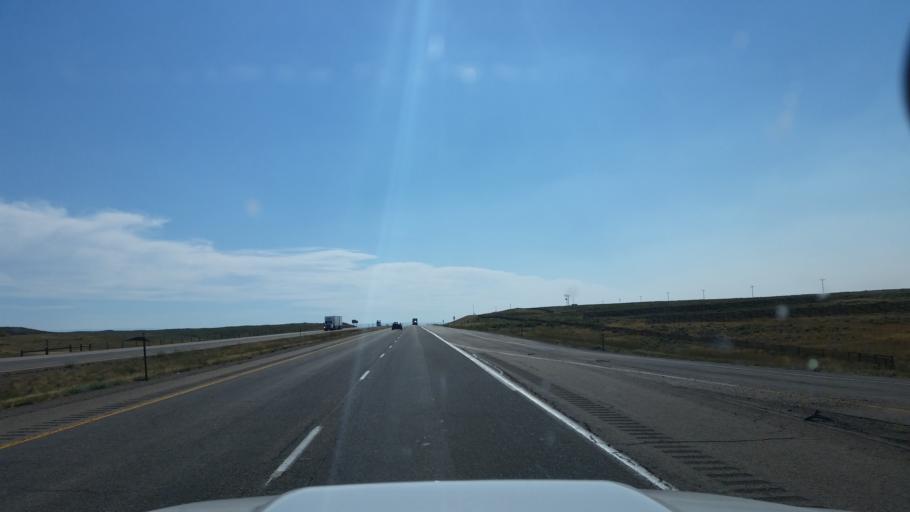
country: US
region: Wyoming
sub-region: Uinta County
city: Lyman
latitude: 41.4326
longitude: -110.1105
